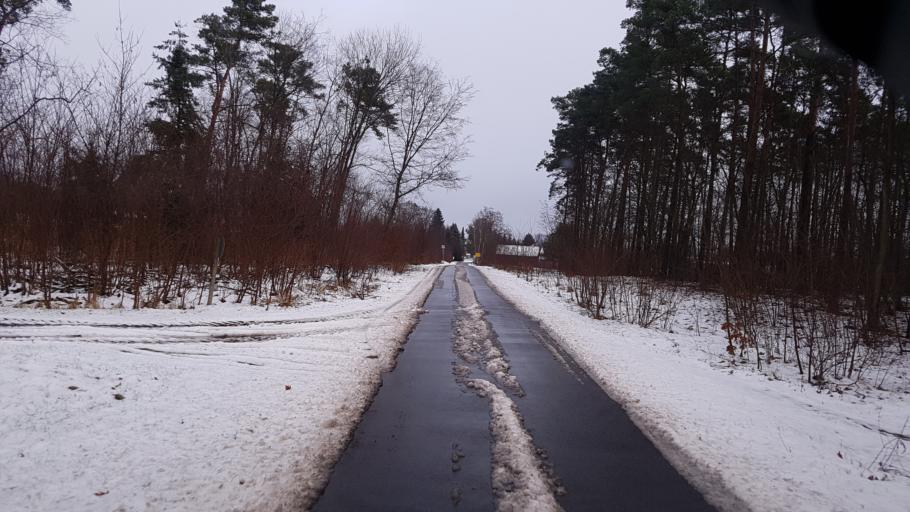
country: DE
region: Brandenburg
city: Straupitz
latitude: 51.9759
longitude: 14.1840
